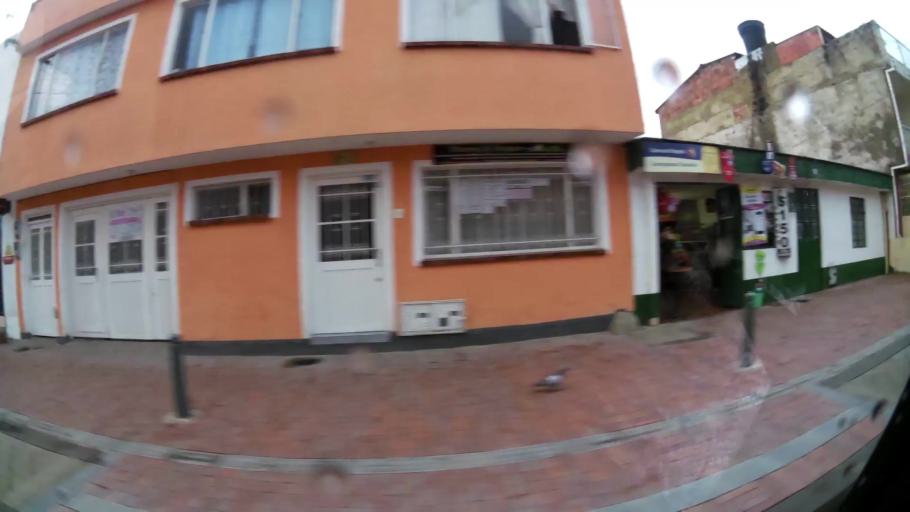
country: CO
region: Cundinamarca
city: Chia
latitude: 4.8648
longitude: -74.0611
